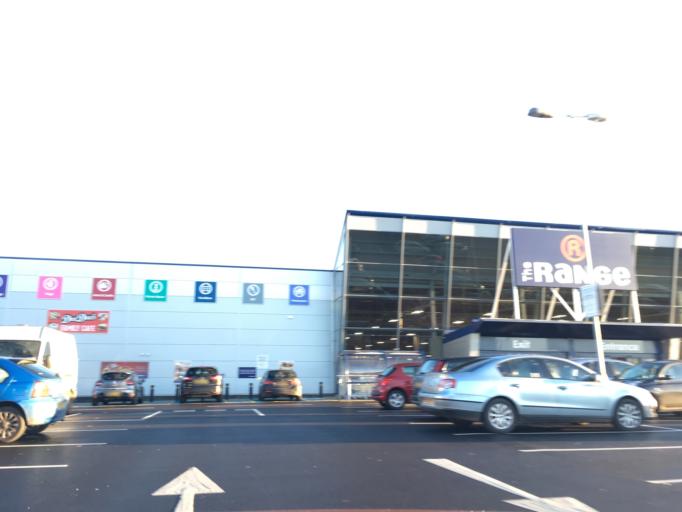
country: GB
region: England
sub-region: South Gloucestershire
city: Stoke Gifford
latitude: 51.5081
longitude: -2.5509
